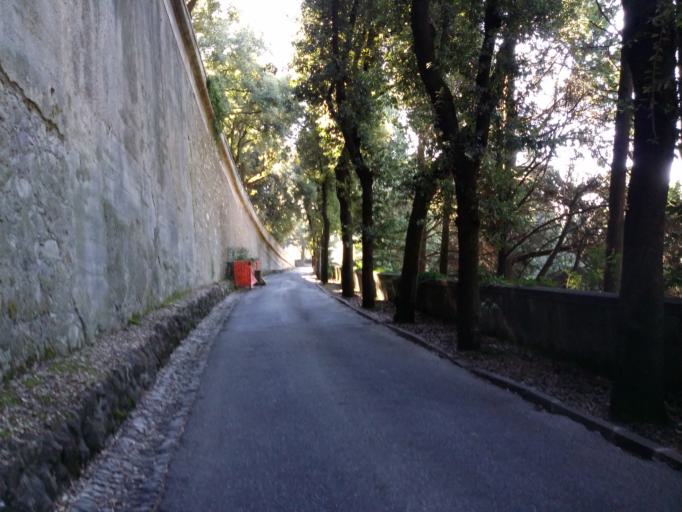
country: IT
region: Liguria
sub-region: Provincia di Genova
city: Genoa
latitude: 44.4319
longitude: 8.9485
